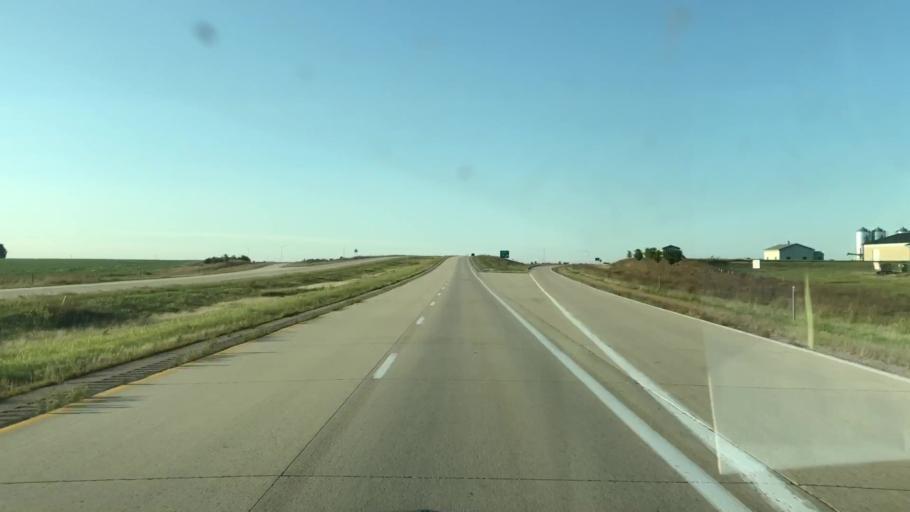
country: US
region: Iowa
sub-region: Osceola County
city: Sibley
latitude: 43.4384
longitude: -95.7136
